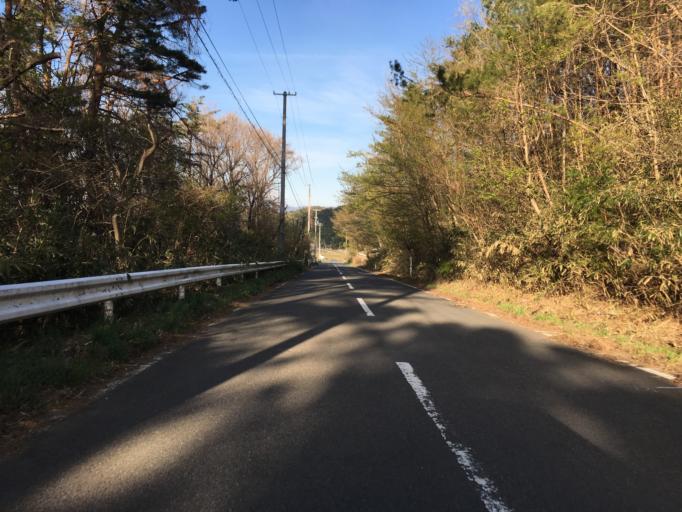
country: JP
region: Fukushima
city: Fukushima-shi
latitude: 37.7049
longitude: 140.3754
